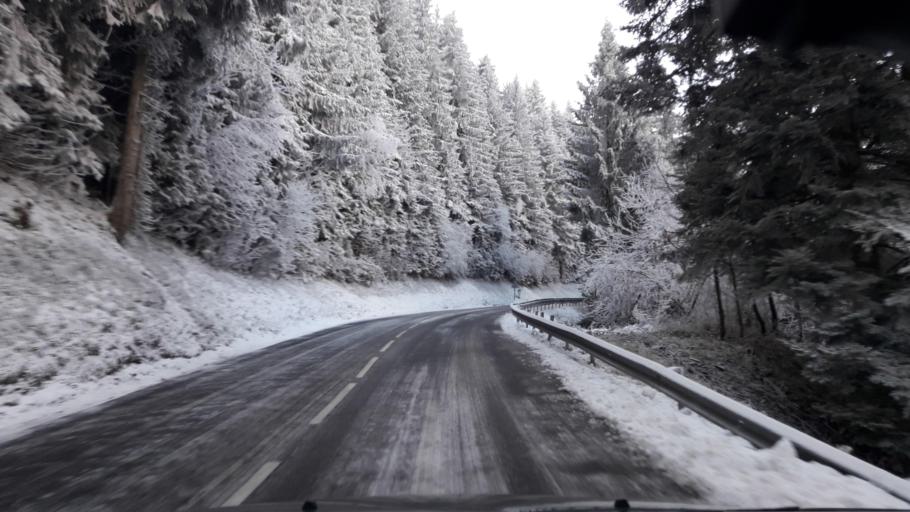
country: FR
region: Rhone-Alpes
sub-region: Departement de l'Isere
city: Allevard
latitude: 45.3963
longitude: 6.1047
